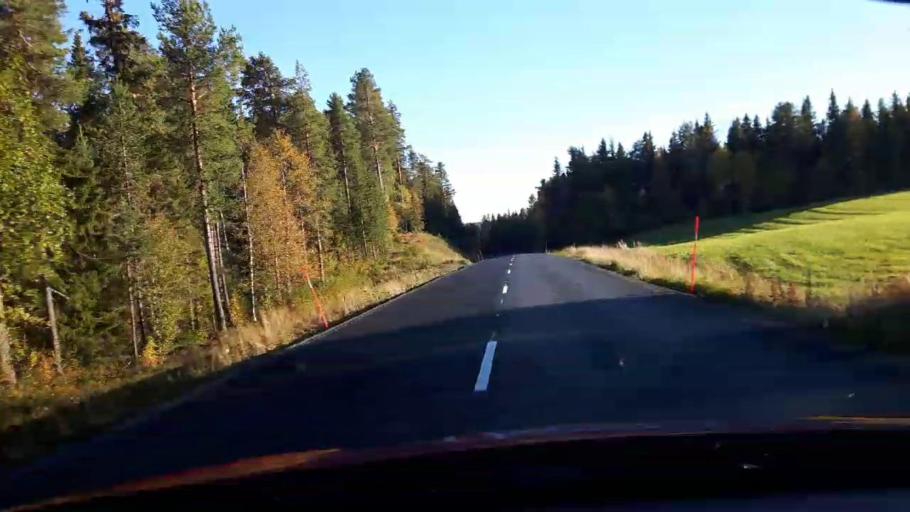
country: SE
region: Jaemtland
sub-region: OEstersunds Kommun
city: Lit
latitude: 63.5287
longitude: 14.8451
